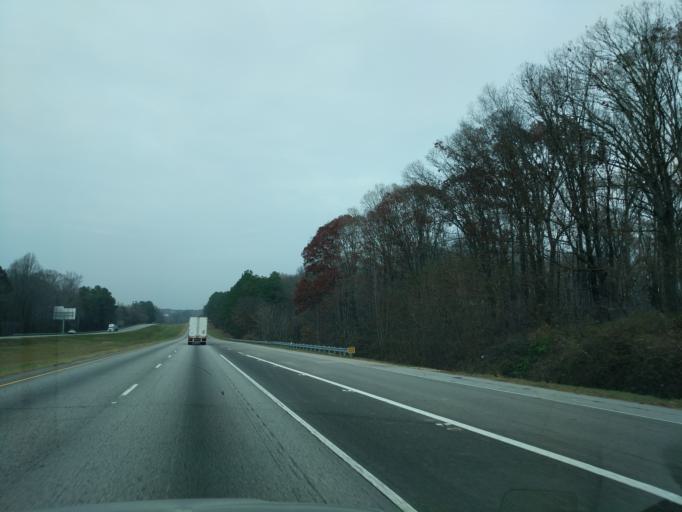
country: US
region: Georgia
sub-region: Franklin County
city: Carnesville
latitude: 34.3521
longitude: -83.3058
